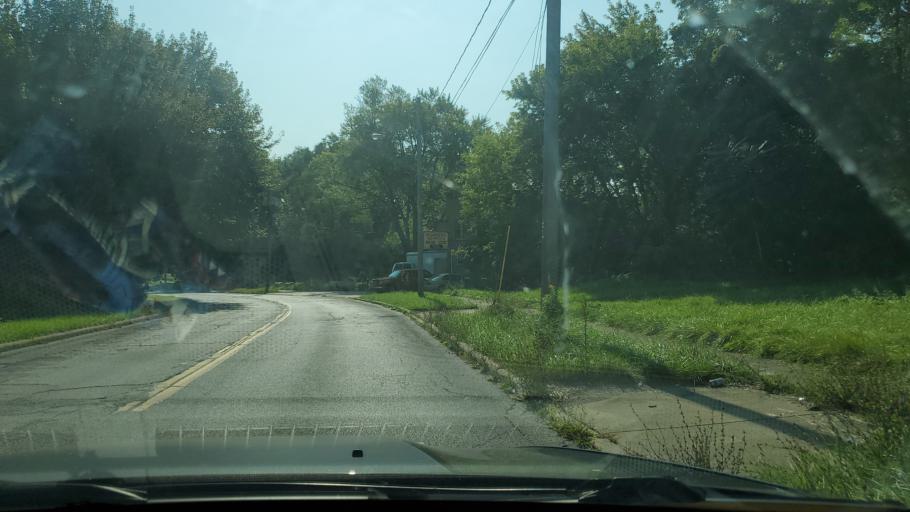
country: US
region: Ohio
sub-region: Mahoning County
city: Youngstown
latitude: 41.1153
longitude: -80.6873
